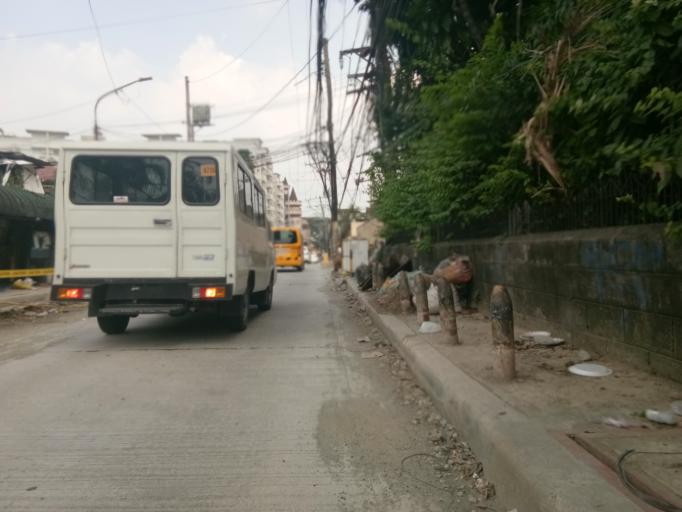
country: PH
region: Metro Manila
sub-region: San Juan
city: San Juan
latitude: 14.6132
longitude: 121.0464
